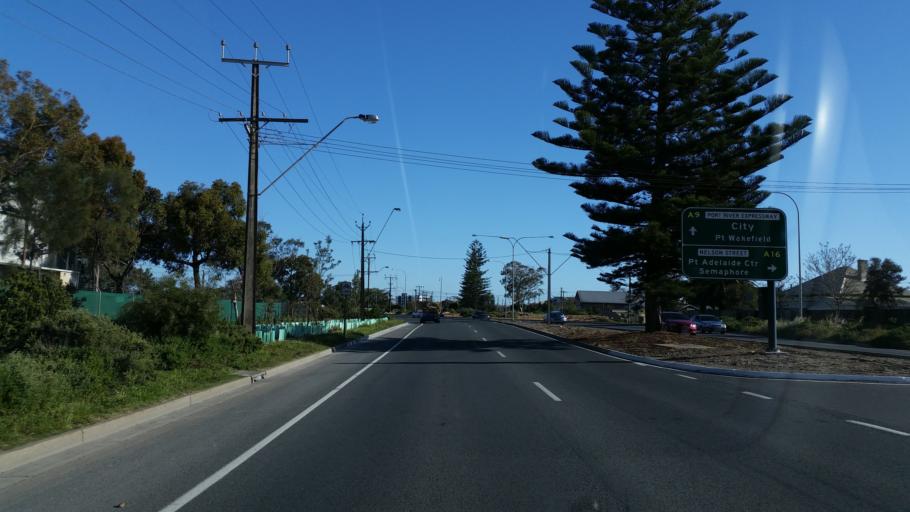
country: AU
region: South Australia
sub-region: Port Adelaide Enfield
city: Birkenhead
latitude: -34.8358
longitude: 138.5019
